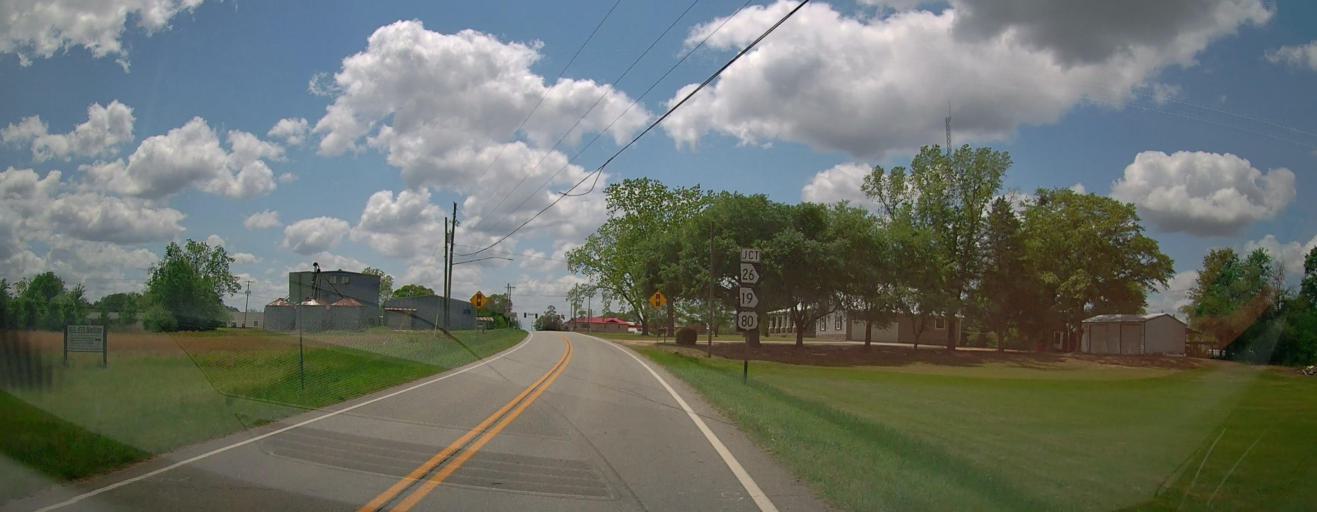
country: US
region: Georgia
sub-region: Laurens County
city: Dublin
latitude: 32.5445
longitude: -83.0694
